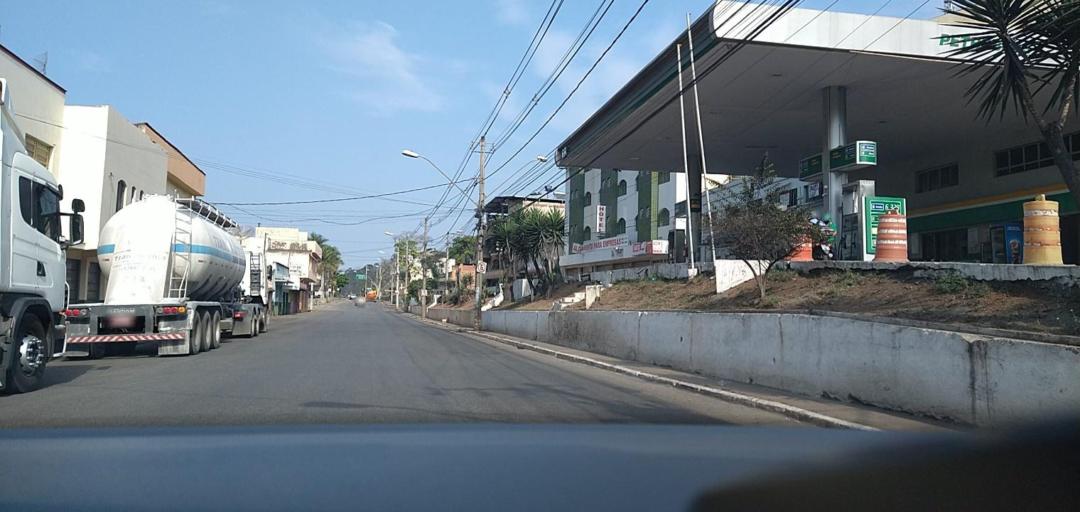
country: BR
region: Minas Gerais
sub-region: Joao Monlevade
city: Joao Monlevade
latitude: -19.8146
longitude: -43.1568
